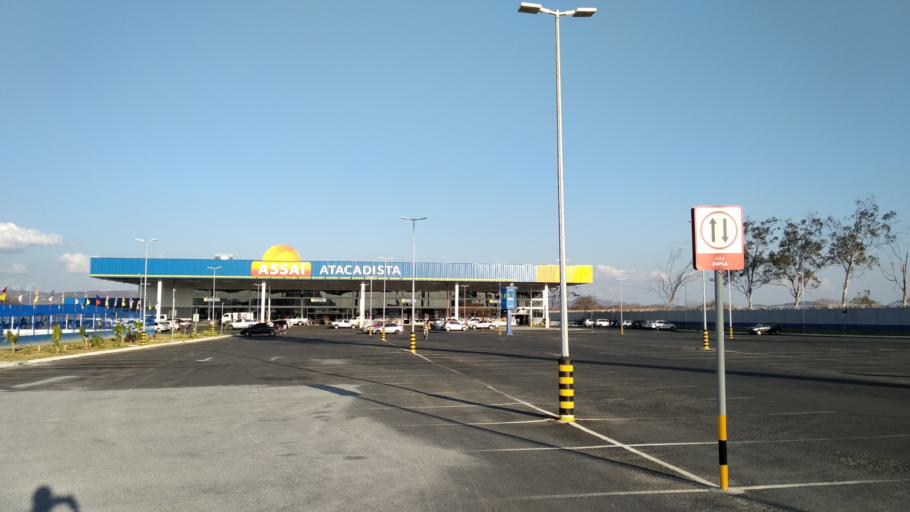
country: BR
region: Bahia
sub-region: Guanambi
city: Guanambi
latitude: -14.1995
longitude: -42.7517
